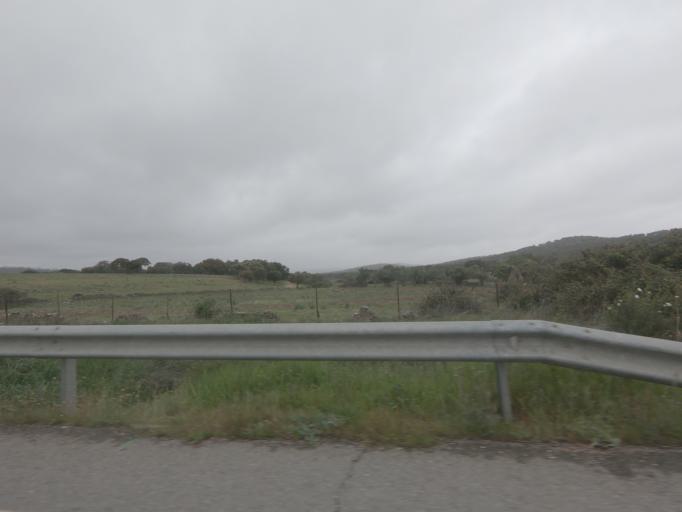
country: ES
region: Extremadura
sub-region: Provincia de Caceres
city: Malpartida de Caceres
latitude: 39.2972
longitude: -6.5185
